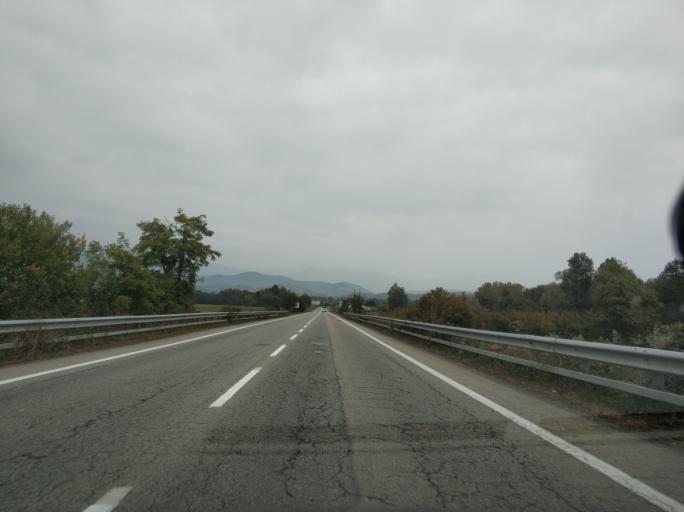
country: IT
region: Piedmont
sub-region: Provincia di Torino
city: Castellamonte
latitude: 45.3757
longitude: 7.7316
